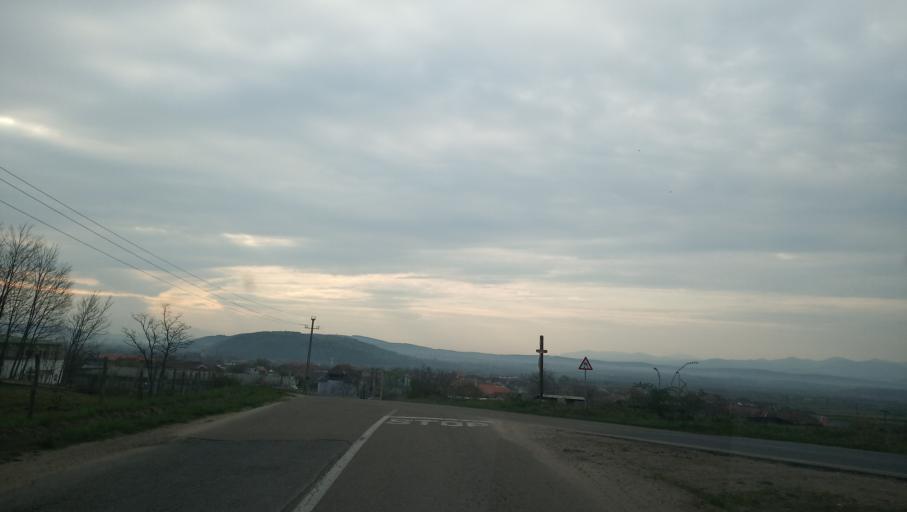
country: RO
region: Bihor
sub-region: Comuna Holod
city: Holod
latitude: 46.7895
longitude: 22.1131
